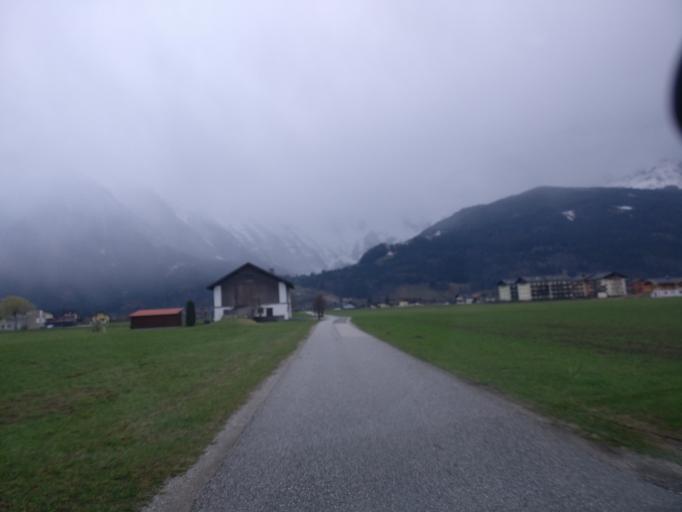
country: AT
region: Salzburg
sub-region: Politischer Bezirk Hallein
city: Kuchl
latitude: 47.6208
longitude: 13.1622
